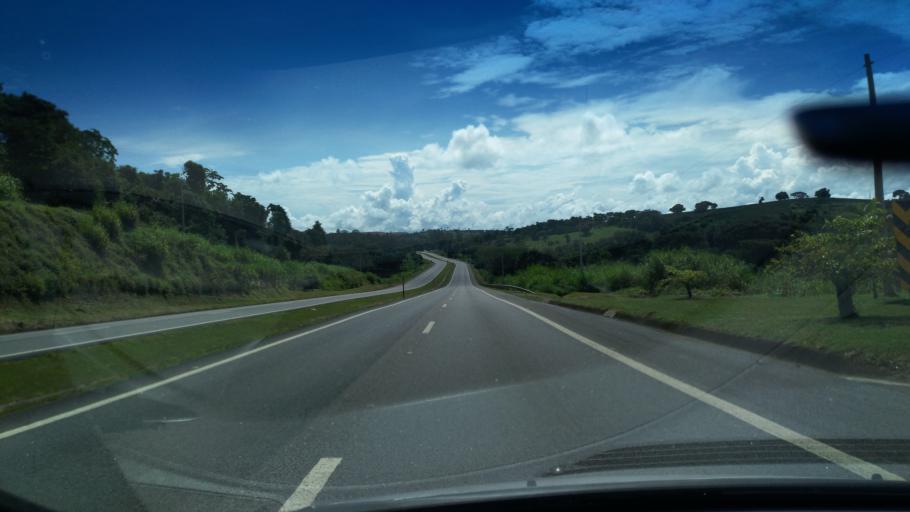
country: BR
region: Sao Paulo
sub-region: Santo Antonio Do Jardim
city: Espirito Santo do Pinhal
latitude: -22.2347
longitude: -46.7978
